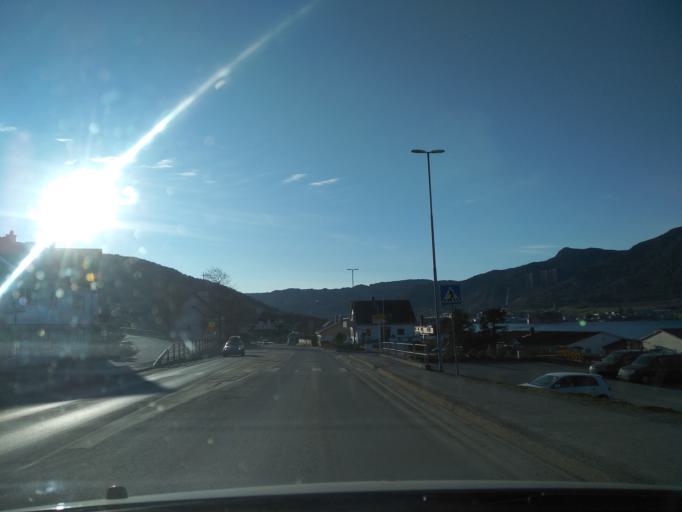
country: NO
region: Rogaland
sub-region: Vindafjord
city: Olen
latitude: 59.6043
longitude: 5.8044
